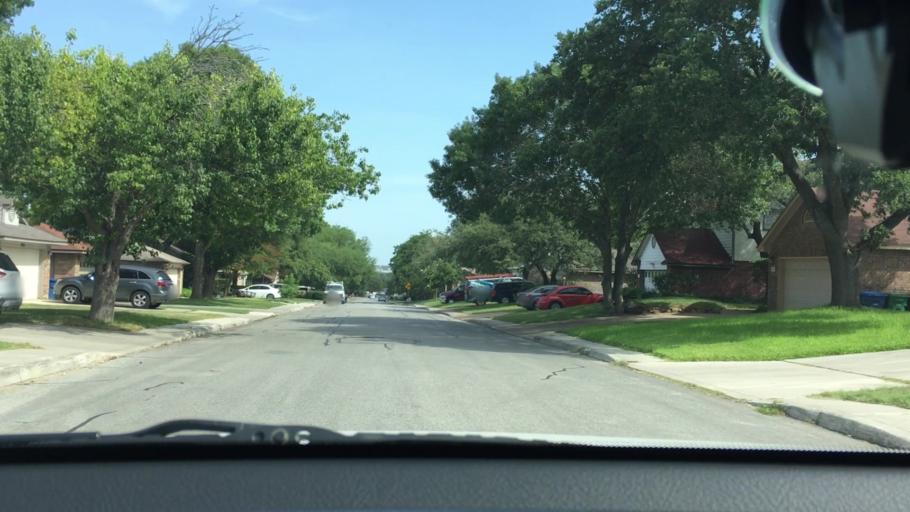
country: US
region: Texas
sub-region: Bexar County
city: Live Oak
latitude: 29.5819
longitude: -98.3770
